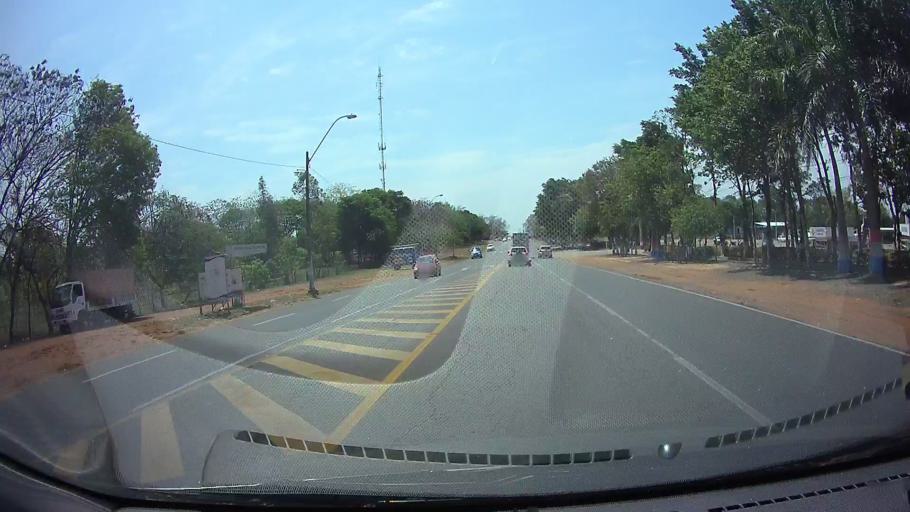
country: PY
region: Central
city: Capiata
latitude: -25.4051
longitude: -57.4623
